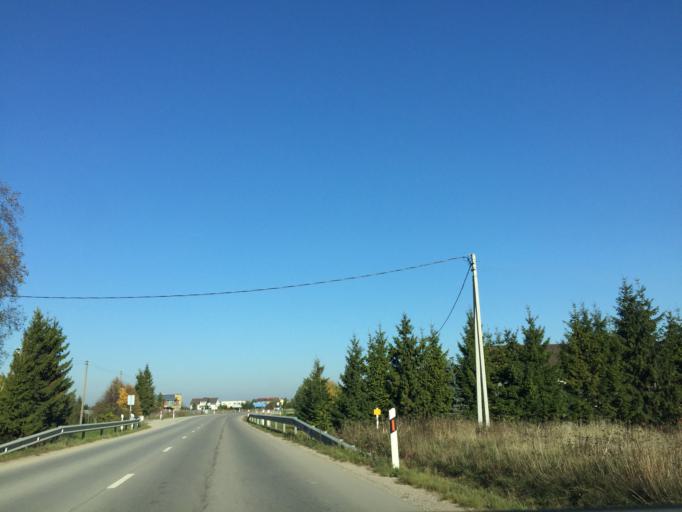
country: LT
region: Klaipedos apskritis
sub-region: Klaipeda
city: Klaipeda
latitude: 55.7544
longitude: 21.1926
